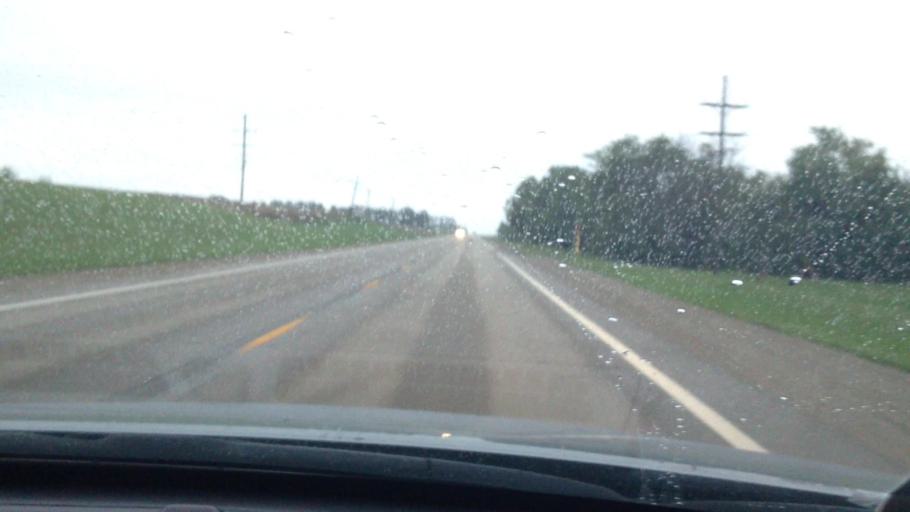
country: US
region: Kansas
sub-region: Brown County
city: Hiawatha
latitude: 39.8252
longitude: -95.5270
